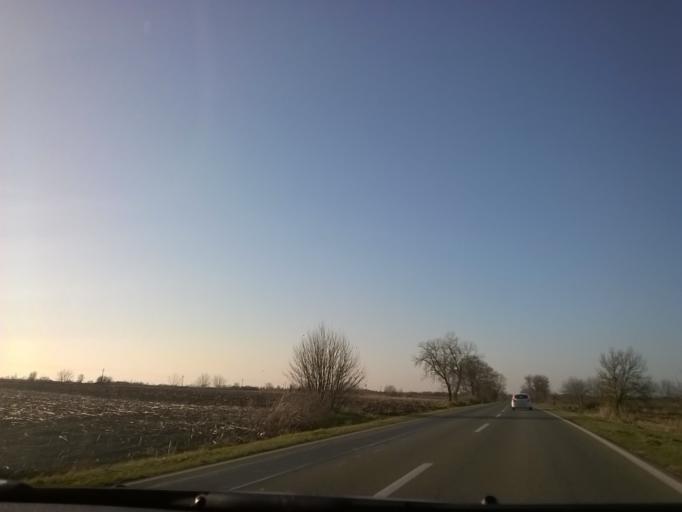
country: RS
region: Autonomna Pokrajina Vojvodina
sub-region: Juznobanatski Okrug
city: Alibunar
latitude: 45.0644
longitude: 20.9777
